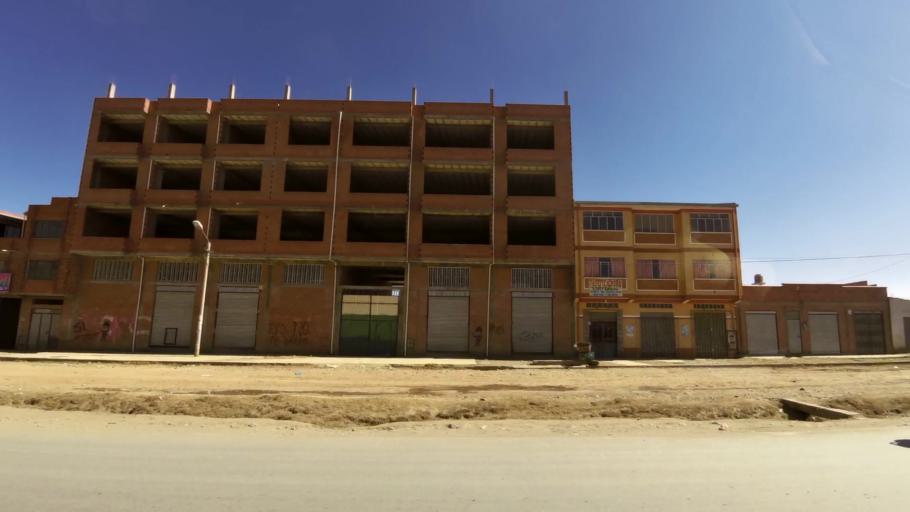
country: BO
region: La Paz
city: La Paz
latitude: -16.5609
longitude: -68.2153
